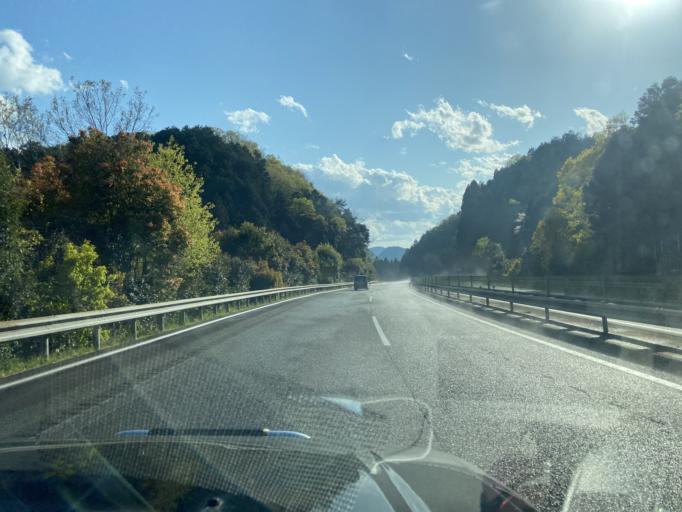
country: JP
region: Kyoto
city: Fukuchiyama
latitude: 35.2053
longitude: 135.1626
